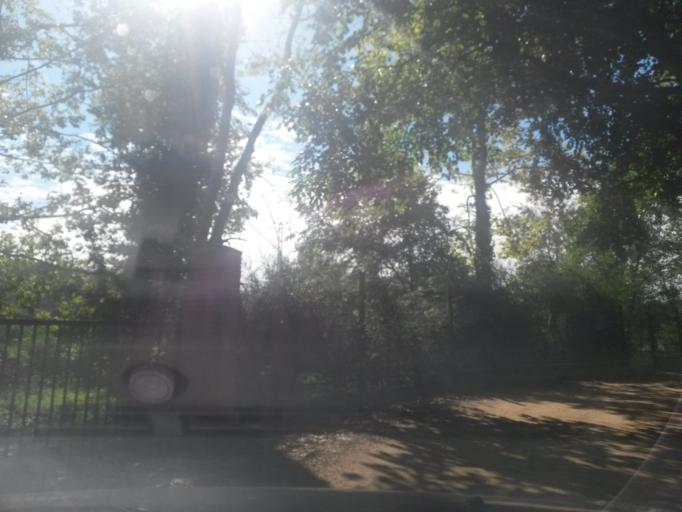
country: ES
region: Catalonia
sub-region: Provincia de Girona
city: la Cellera de Ter
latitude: 41.9862
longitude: 2.6198
